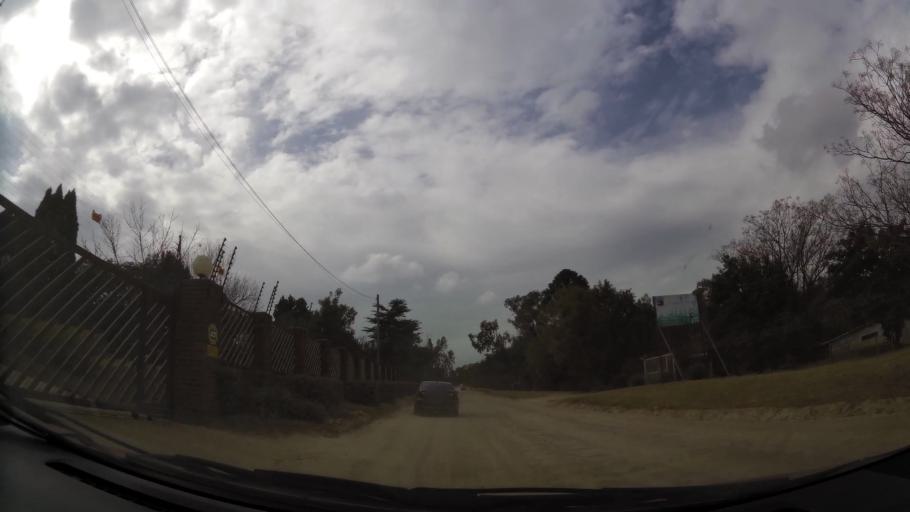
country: ZA
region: Gauteng
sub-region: West Rand District Municipality
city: Muldersdriseloop
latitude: -26.0662
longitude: 27.8910
